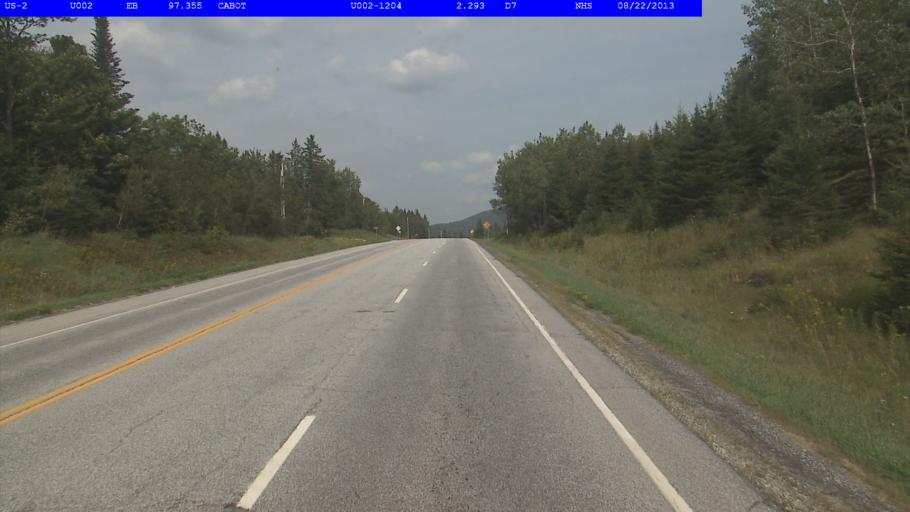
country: US
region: Vermont
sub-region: Caledonia County
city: Hardwick
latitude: 44.3672
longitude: -72.2809
